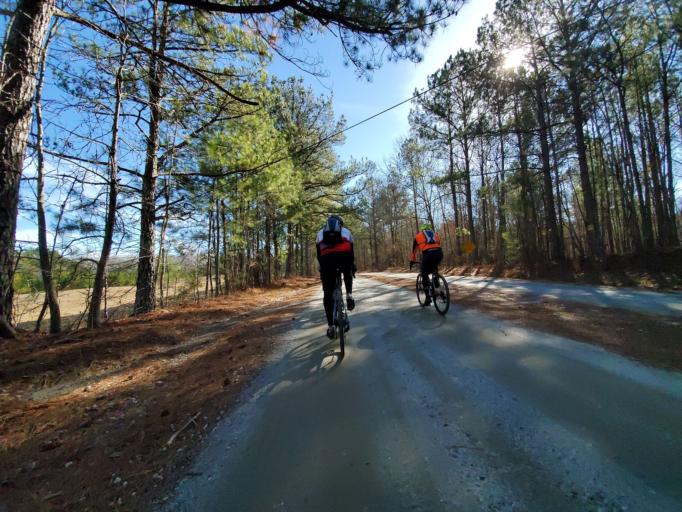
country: US
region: Georgia
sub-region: Fulton County
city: Chattahoochee Hills
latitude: 33.5764
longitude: -84.7840
